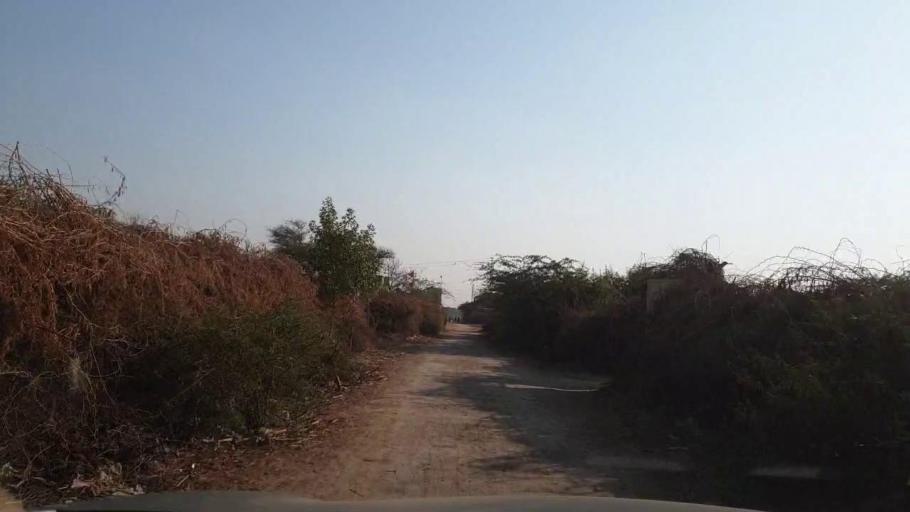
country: PK
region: Sindh
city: Tando Allahyar
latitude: 25.5050
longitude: 68.8500
